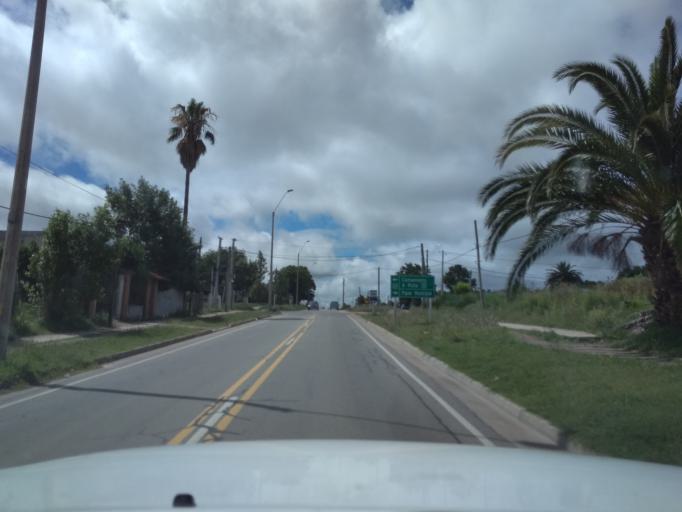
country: UY
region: Canelones
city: Pando
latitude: -34.7107
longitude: -55.9641
